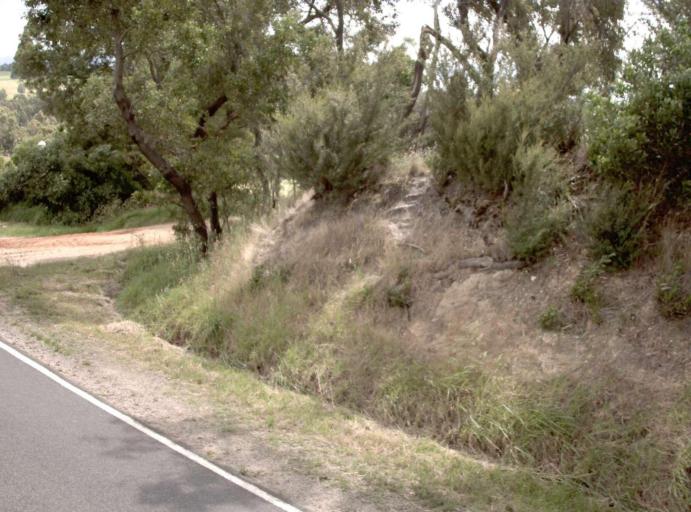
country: AU
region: Victoria
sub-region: Latrobe
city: Moe
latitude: -38.0953
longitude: 146.1570
